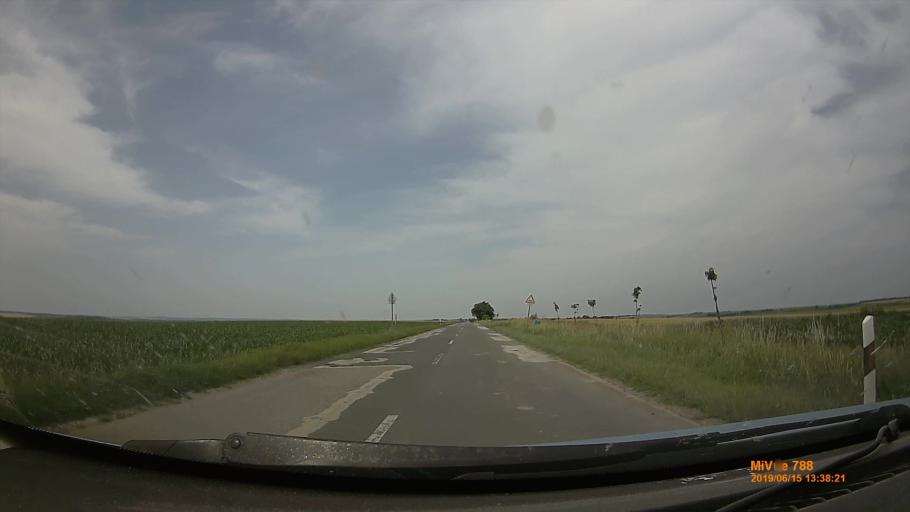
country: HU
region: Tolna
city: Tamasi
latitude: 46.6138
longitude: 18.2058
